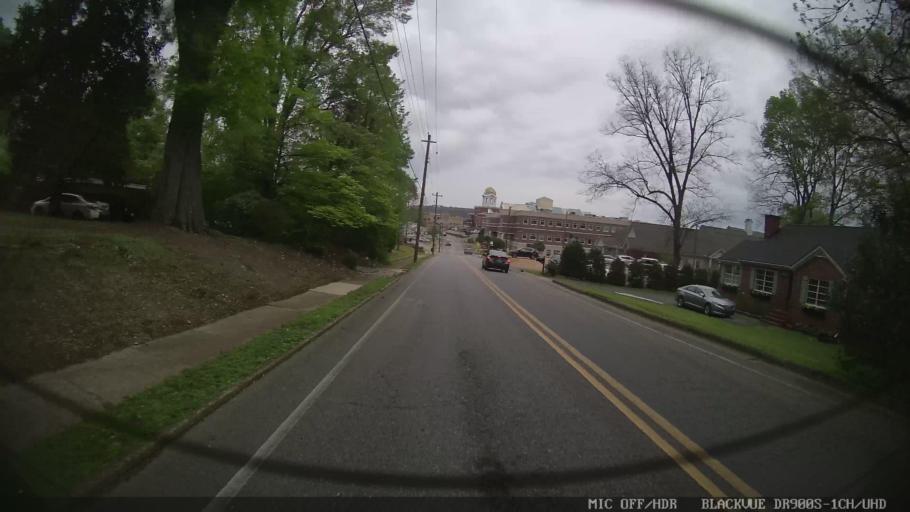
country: US
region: Georgia
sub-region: Bartow County
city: Cartersville
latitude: 34.1661
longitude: -84.8016
